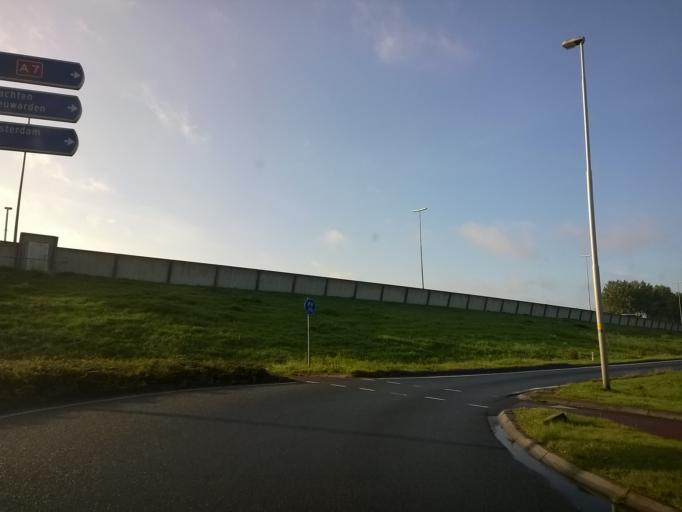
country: NL
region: Groningen
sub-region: Gemeente Groningen
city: Groningen
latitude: 53.1988
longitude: 6.5458
